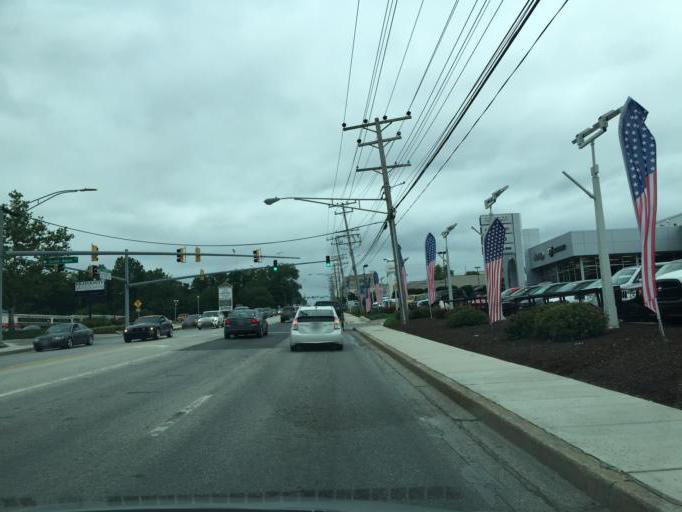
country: US
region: Maryland
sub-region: Baltimore County
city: Cockeysville
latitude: 39.4720
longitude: -76.6399
